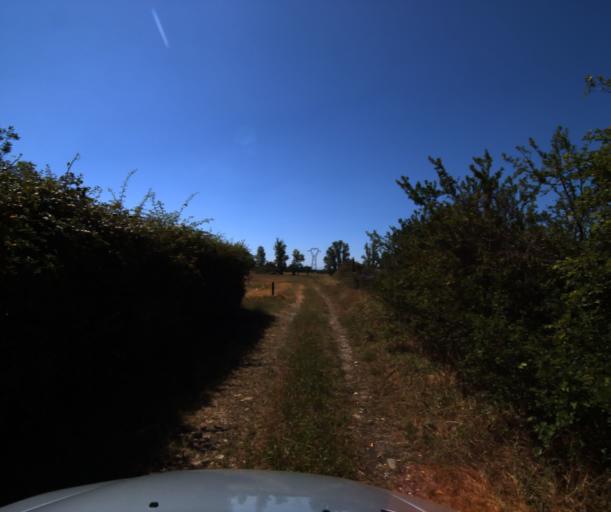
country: FR
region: Midi-Pyrenees
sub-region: Departement de la Haute-Garonne
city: Muret
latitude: 43.4555
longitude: 1.3677
